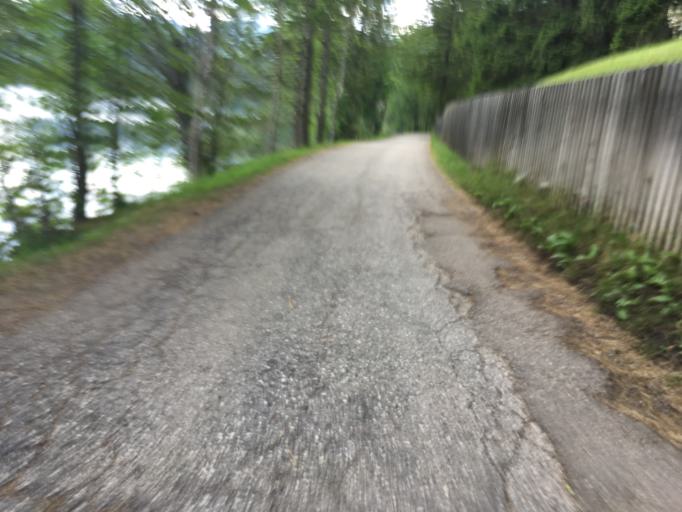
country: AT
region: Lower Austria
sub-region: Politischer Bezirk Lilienfeld
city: Mitterbach am Erlaufsee
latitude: 47.7952
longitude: 15.2714
